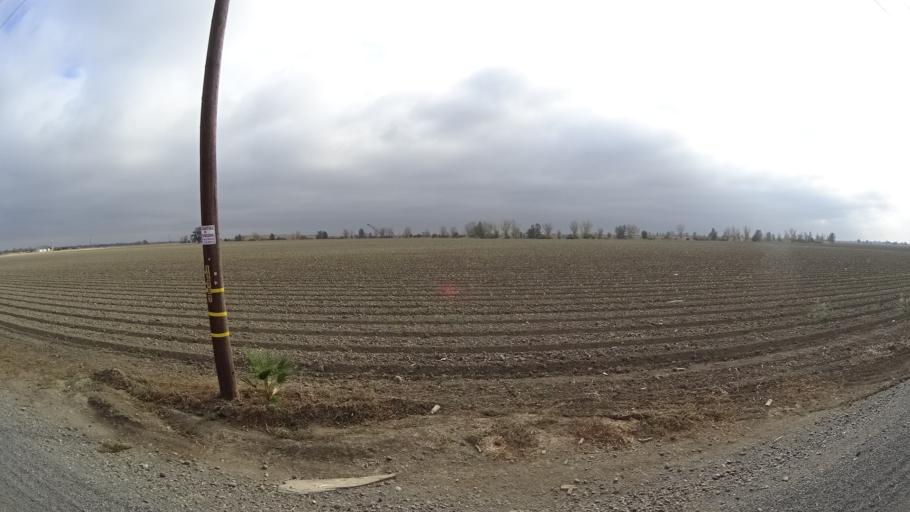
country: US
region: California
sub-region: Yolo County
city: Esparto
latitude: 38.7070
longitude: -122.0136
